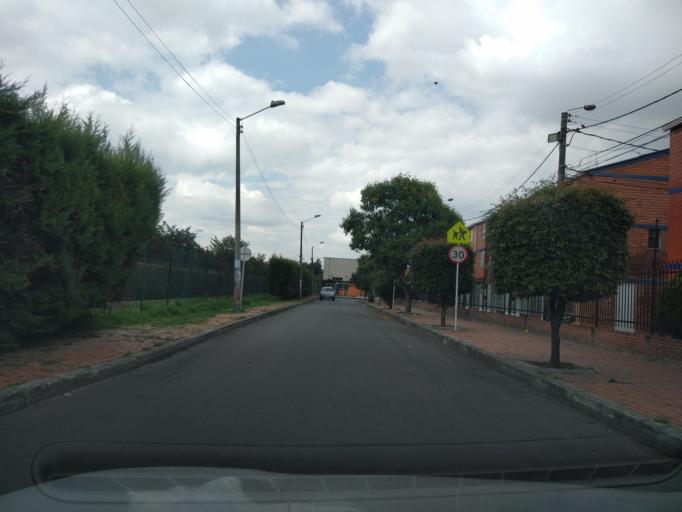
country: CO
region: Cundinamarca
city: Funza
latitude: 4.6710
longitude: -74.1603
